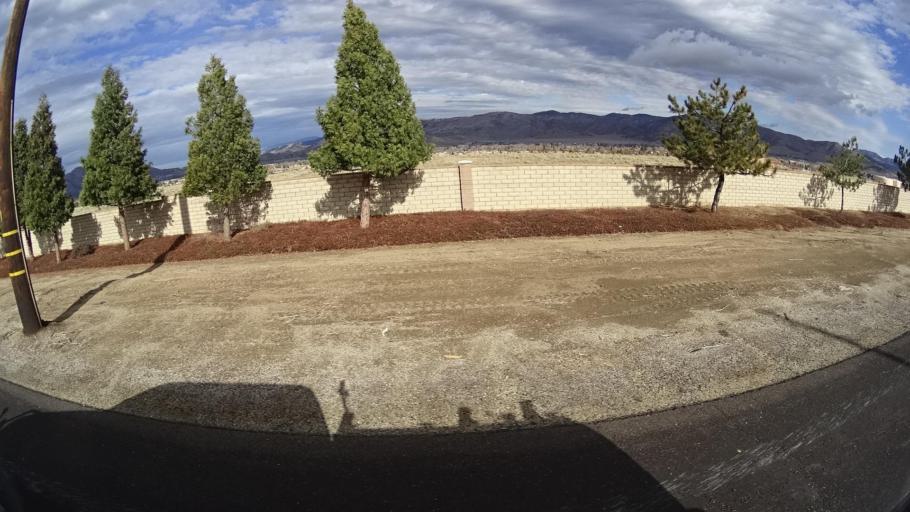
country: US
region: California
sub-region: Kern County
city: Tehachapi
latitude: 35.1096
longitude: -118.4547
